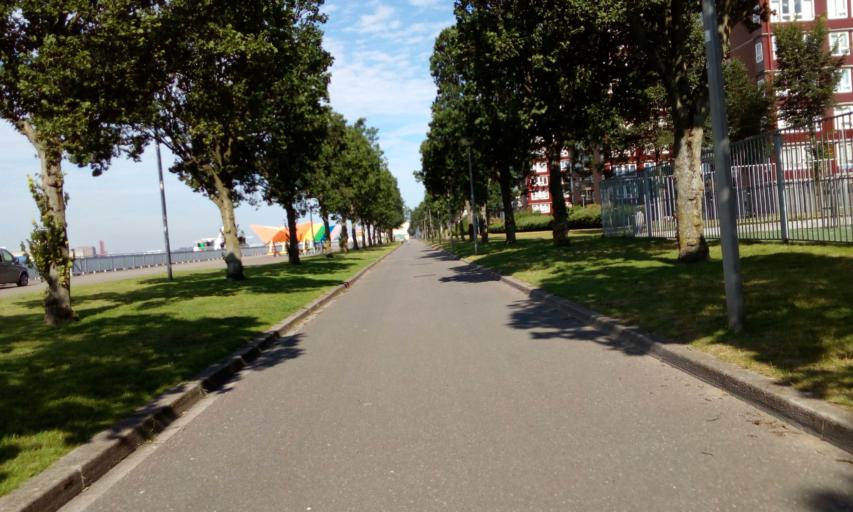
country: NL
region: South Holland
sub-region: Gemeente Rotterdam
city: Delfshaven
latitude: 51.9022
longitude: 4.4470
